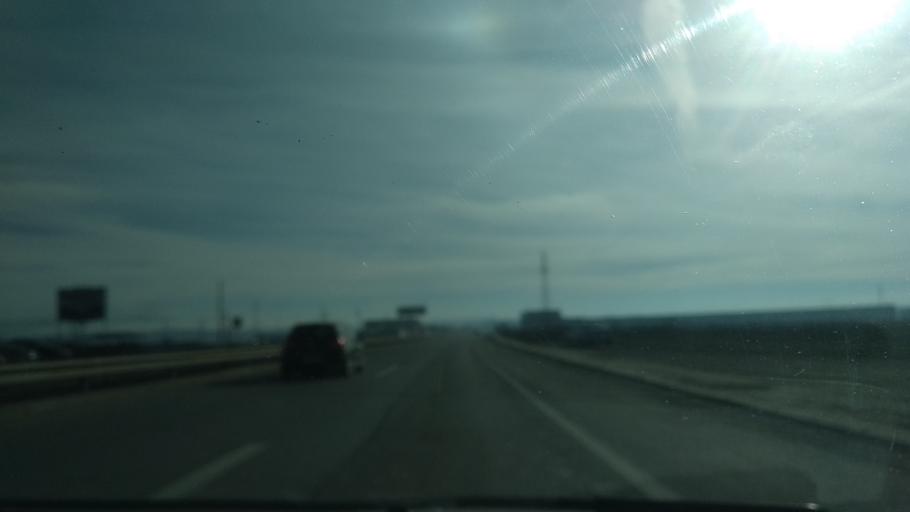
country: XK
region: Pristina
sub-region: Komuna e Obiliqit
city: Obiliq
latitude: 42.7150
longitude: 21.0968
